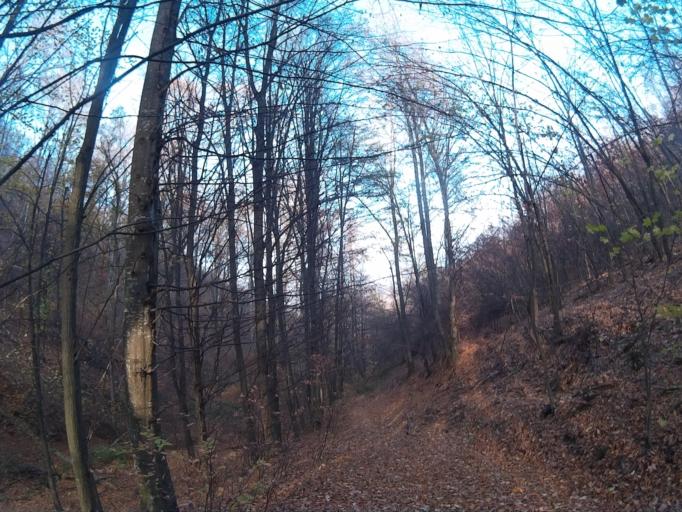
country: HU
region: Heves
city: Belapatfalva
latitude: 48.0615
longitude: 20.4032
